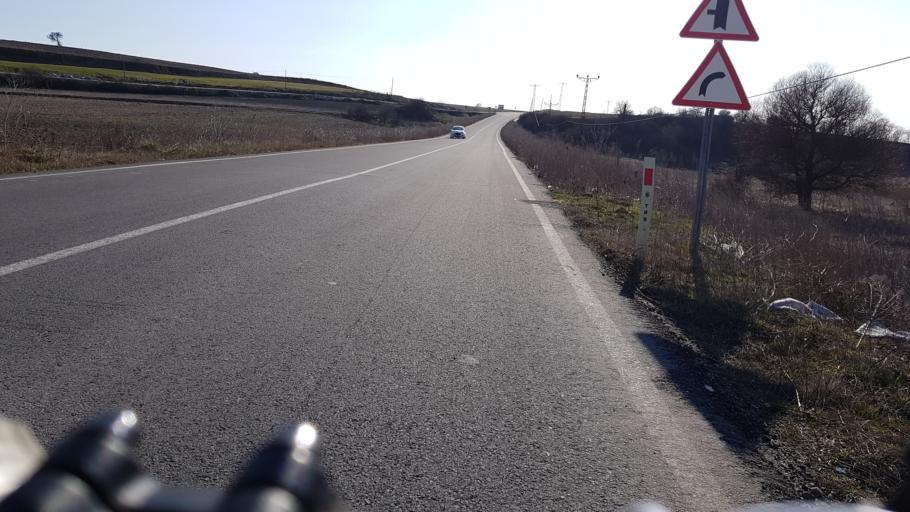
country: TR
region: Tekirdag
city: Velimese
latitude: 41.3571
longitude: 27.8505
